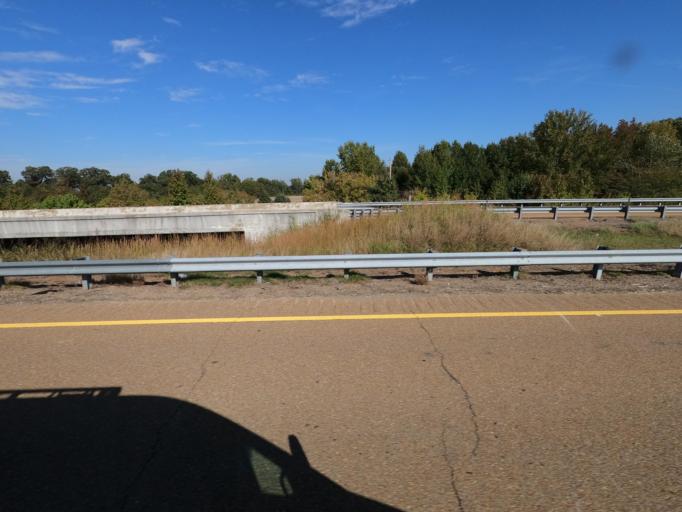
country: US
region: Tennessee
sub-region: Shelby County
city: Lakeland
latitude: 35.3102
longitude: -89.7757
